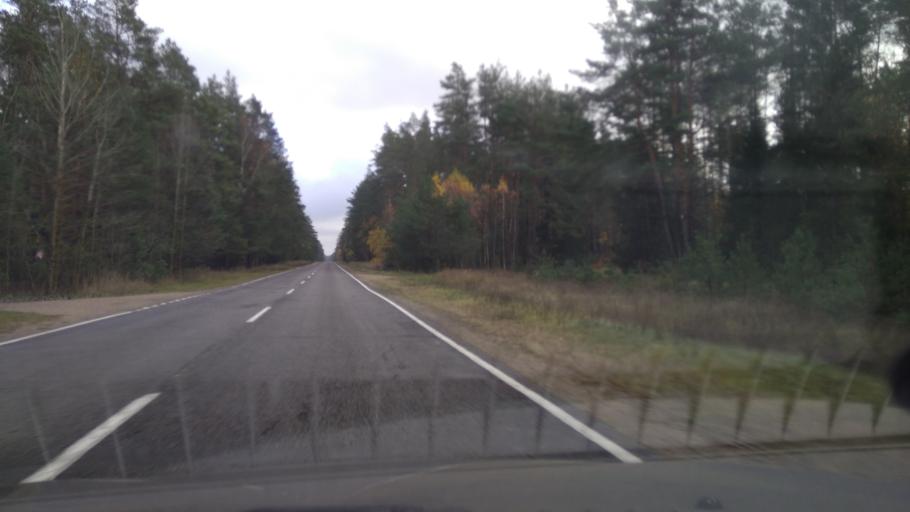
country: BY
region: Minsk
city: Slutsk
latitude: 53.2300
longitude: 27.6917
